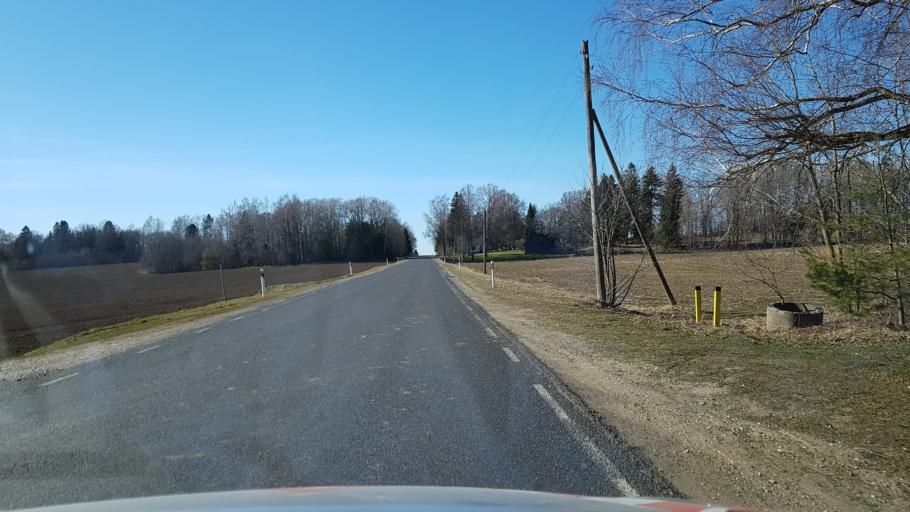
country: EE
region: Laeaene-Virumaa
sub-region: Vinni vald
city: Vinni
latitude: 59.3172
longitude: 26.5121
